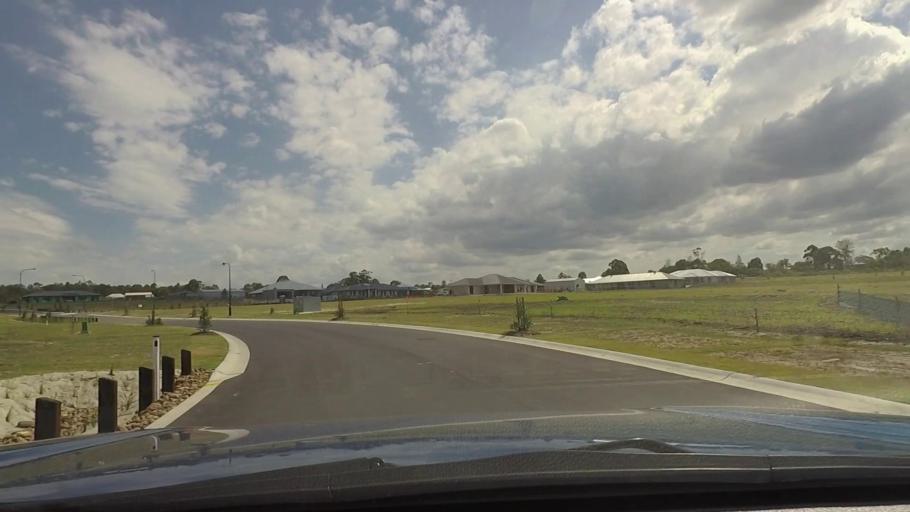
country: AU
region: Queensland
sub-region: Logan
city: North Maclean
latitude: -27.7378
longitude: 152.9509
